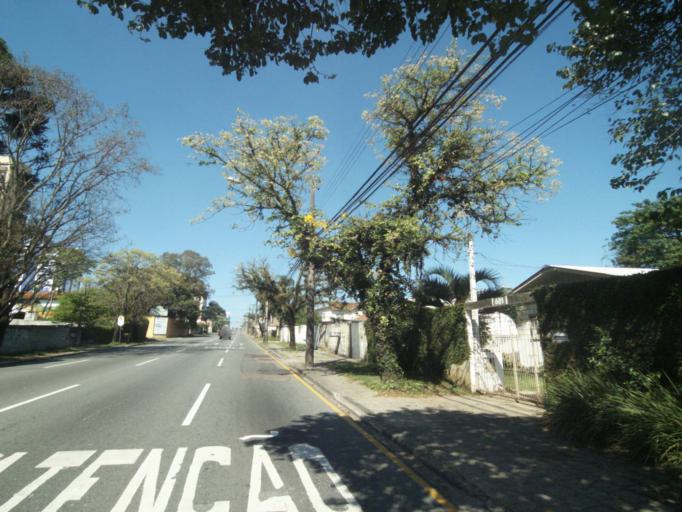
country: BR
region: Parana
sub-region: Curitiba
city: Curitiba
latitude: -25.3825
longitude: -49.2318
